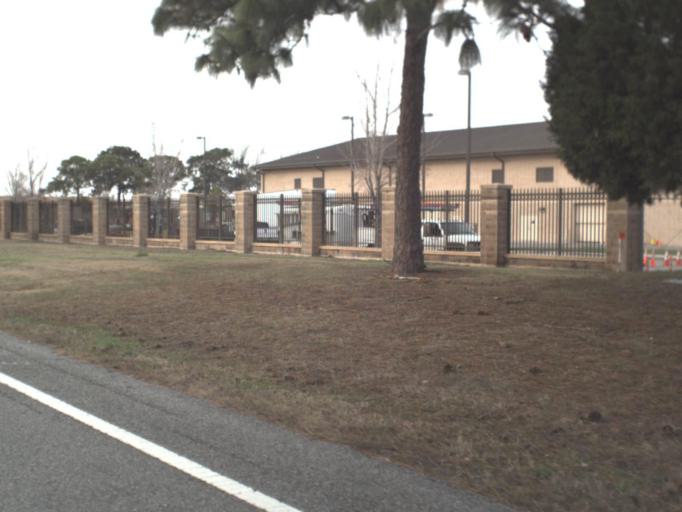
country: US
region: Florida
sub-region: Bay County
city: Tyndall Air Force Base
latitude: 30.0697
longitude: -85.5898
